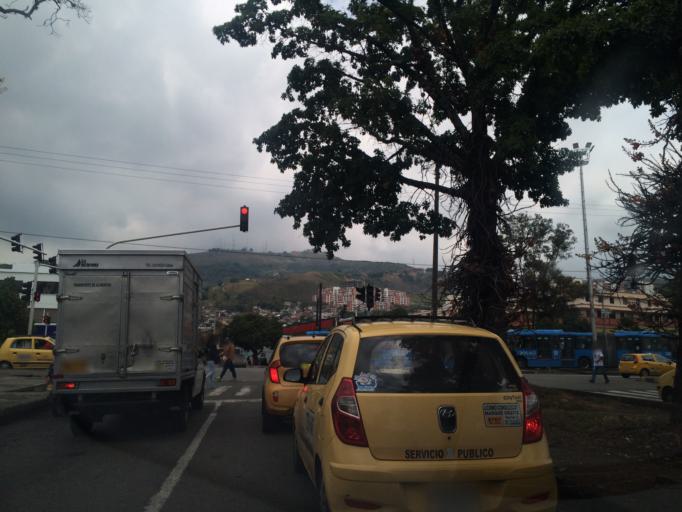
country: CO
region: Valle del Cauca
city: Cali
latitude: 3.4242
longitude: -76.5462
